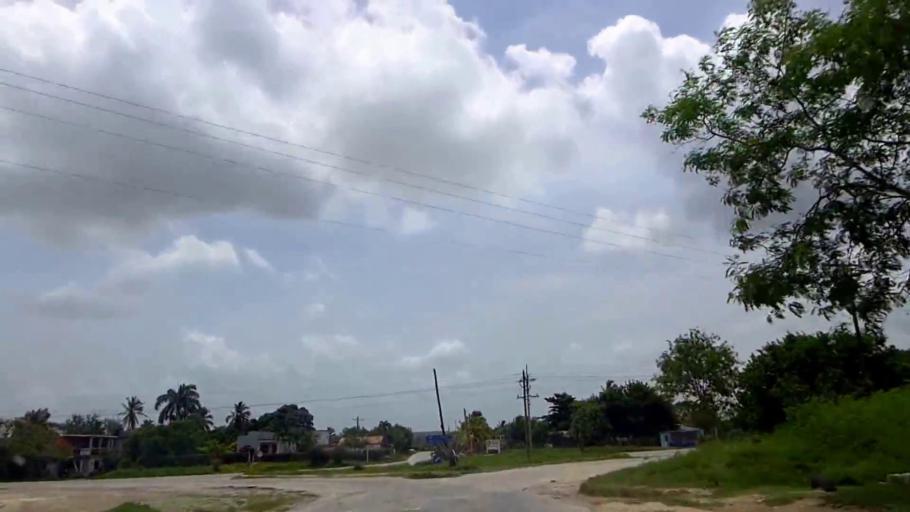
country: CU
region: Holguin
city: Cacocum
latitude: 20.8068
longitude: -76.2917
